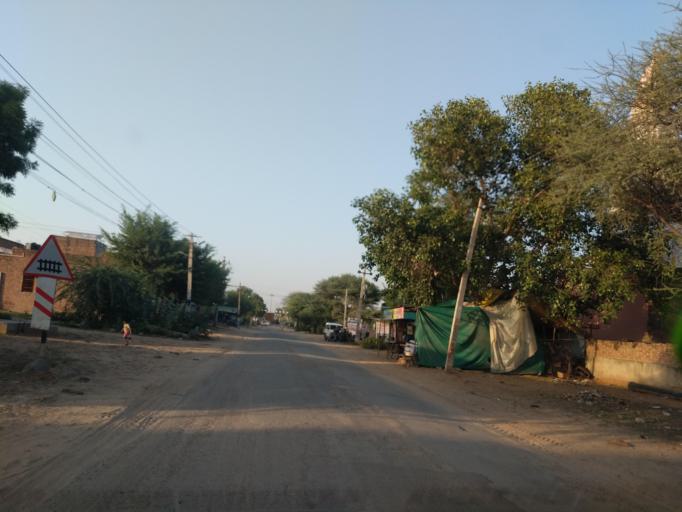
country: IN
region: Rajasthan
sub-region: Churu
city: Rajgarh
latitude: 28.6238
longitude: 75.3797
